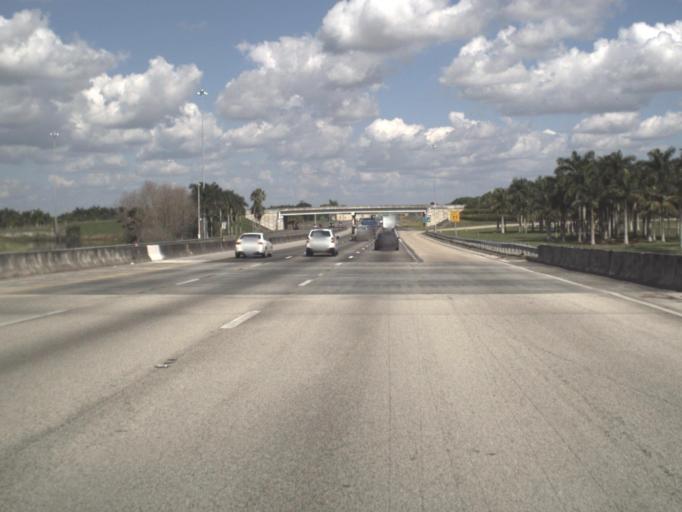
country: US
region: Florida
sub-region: Palm Beach County
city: Boca Del Mar
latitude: 26.3712
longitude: -80.1707
